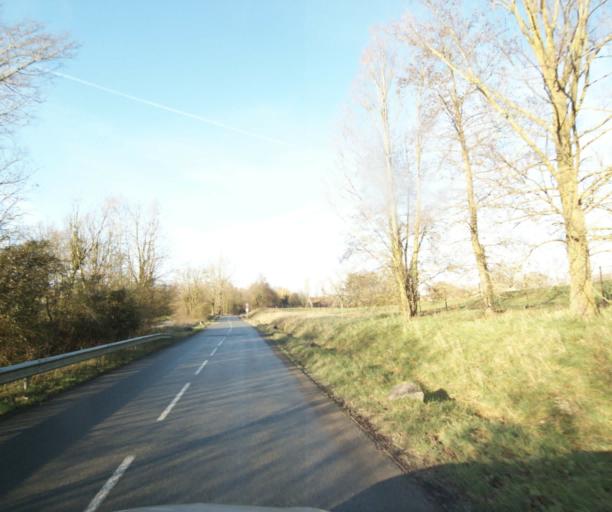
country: FR
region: Nord-Pas-de-Calais
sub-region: Departement du Nord
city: Curgies
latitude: 50.3279
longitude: 3.5950
